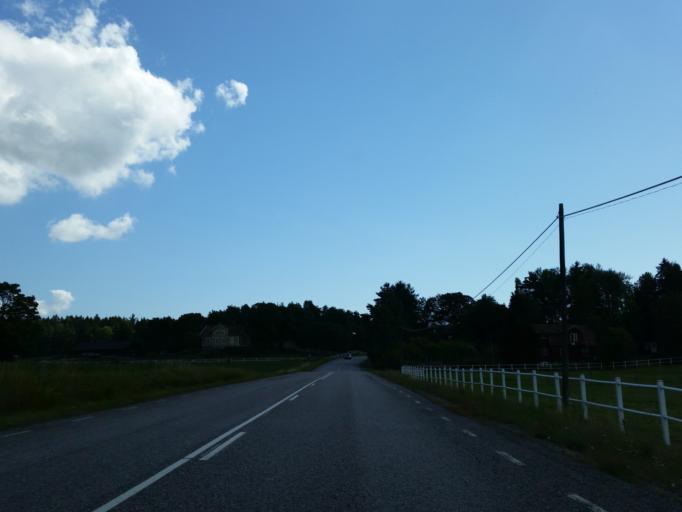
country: SE
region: Soedermanland
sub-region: Trosa Kommun
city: Vagnharad
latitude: 59.0032
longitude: 17.6001
